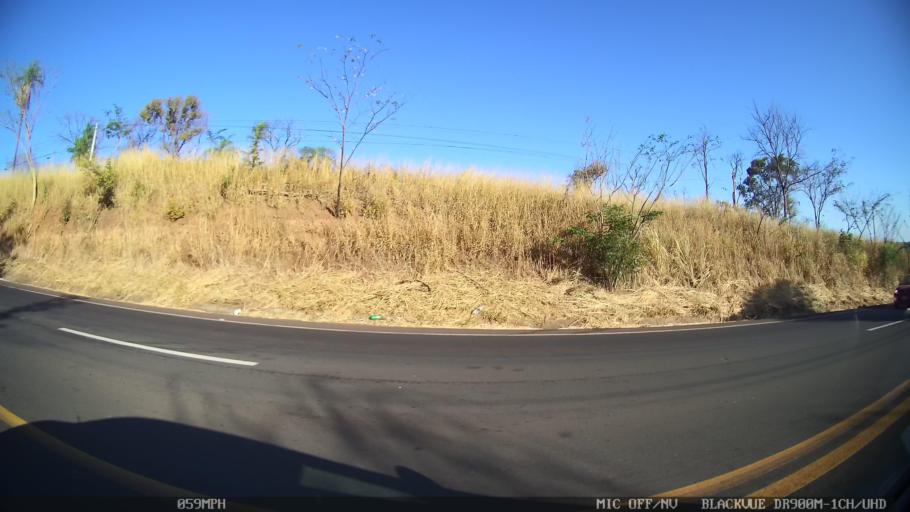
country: BR
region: Sao Paulo
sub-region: Olimpia
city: Olimpia
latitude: -20.7051
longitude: -48.9532
